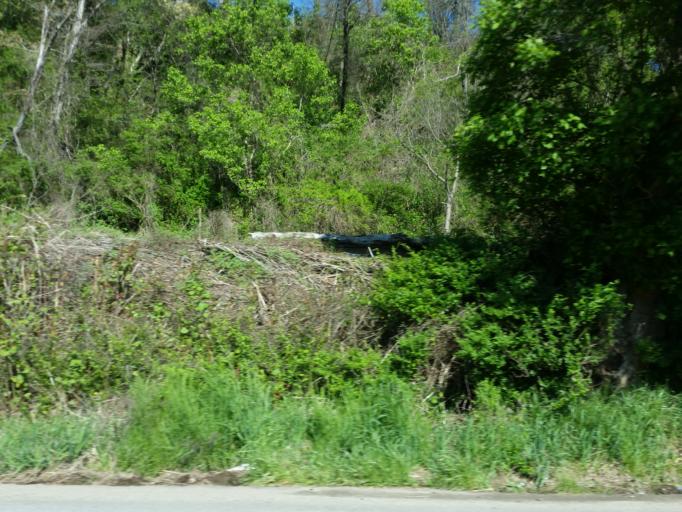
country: US
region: North Carolina
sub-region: Buncombe County
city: Asheville
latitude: 35.5931
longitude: -82.5718
